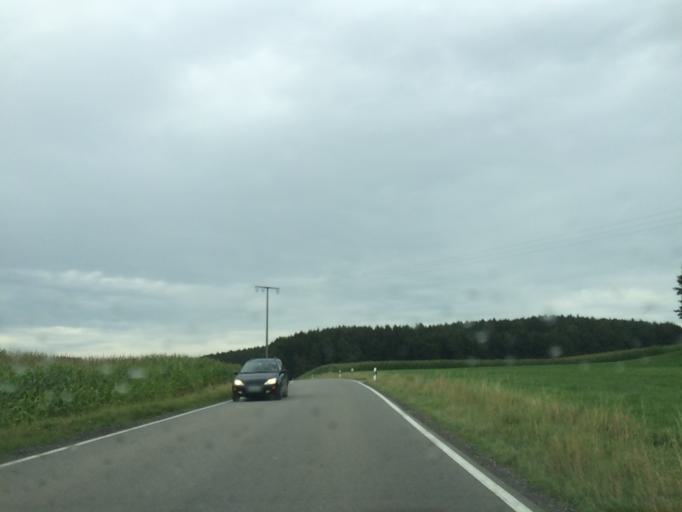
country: DE
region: Baden-Wuerttemberg
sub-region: Tuebingen Region
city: Bad Waldsee
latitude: 47.9461
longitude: 9.7726
